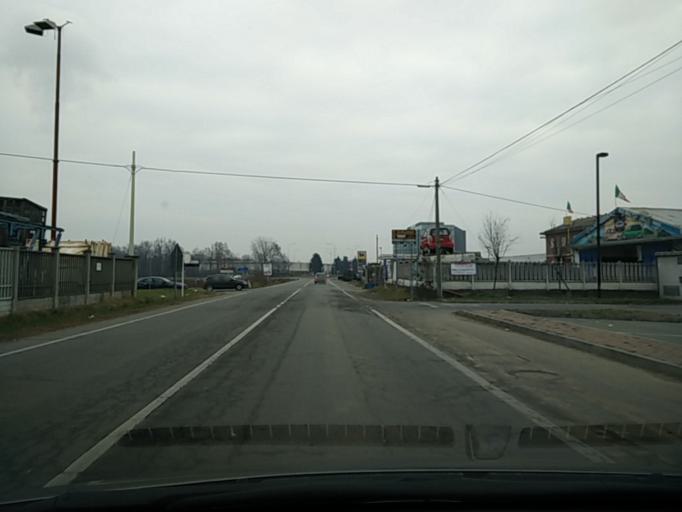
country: IT
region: Piedmont
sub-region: Provincia di Torino
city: Leini
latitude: 45.1566
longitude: 7.7210
